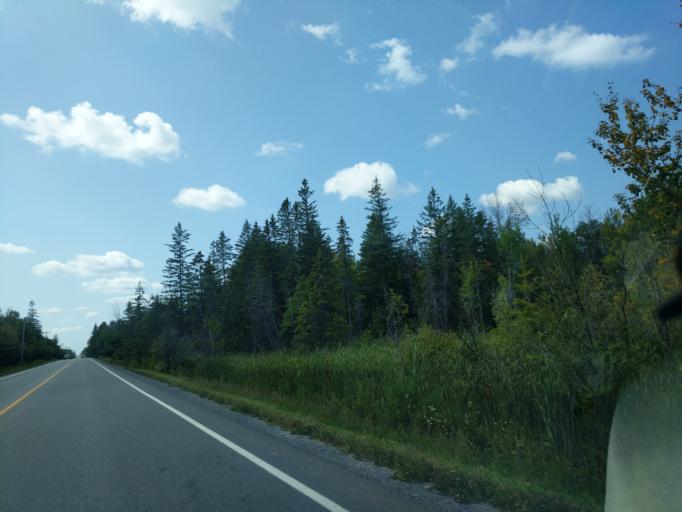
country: CA
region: Ontario
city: Bells Corners
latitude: 45.4413
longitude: -75.8262
